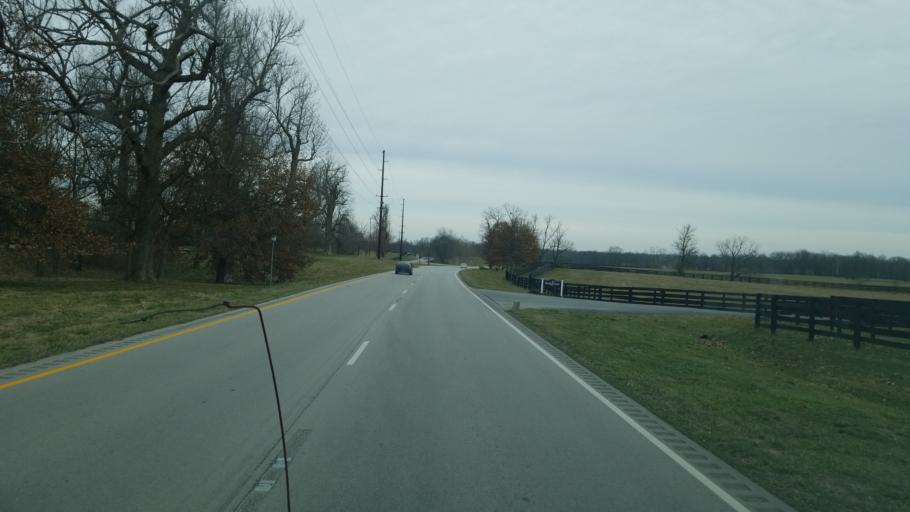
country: US
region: Kentucky
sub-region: Bourbon County
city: Paris
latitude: 38.1640
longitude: -84.3214
